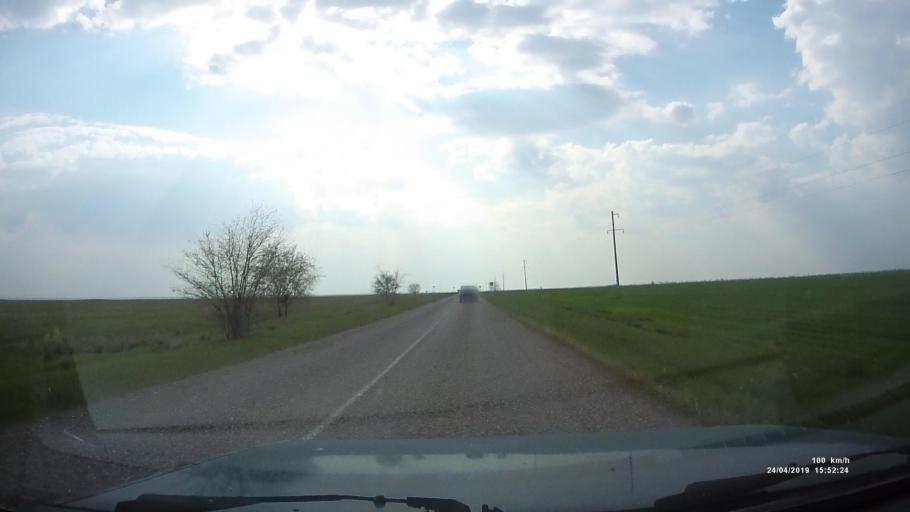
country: RU
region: Kalmykiya
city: Yashalta
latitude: 46.6042
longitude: 42.5887
